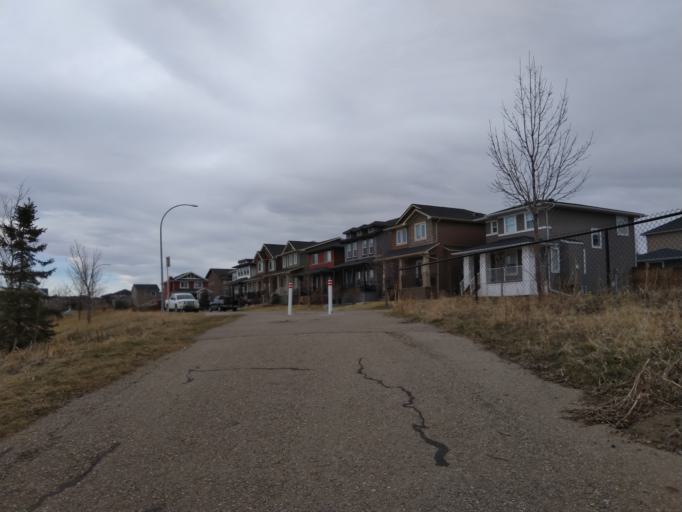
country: CA
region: Alberta
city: Calgary
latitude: 51.1738
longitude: -114.1013
